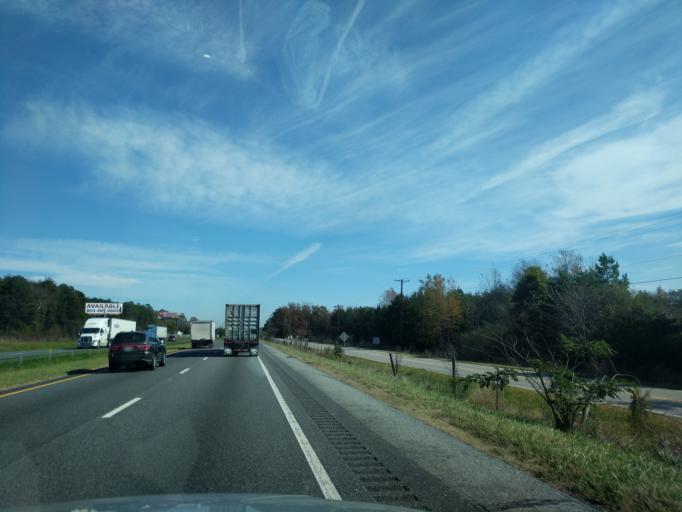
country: US
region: South Carolina
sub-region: Cherokee County
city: Gaffney
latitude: 35.0973
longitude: -81.6537
